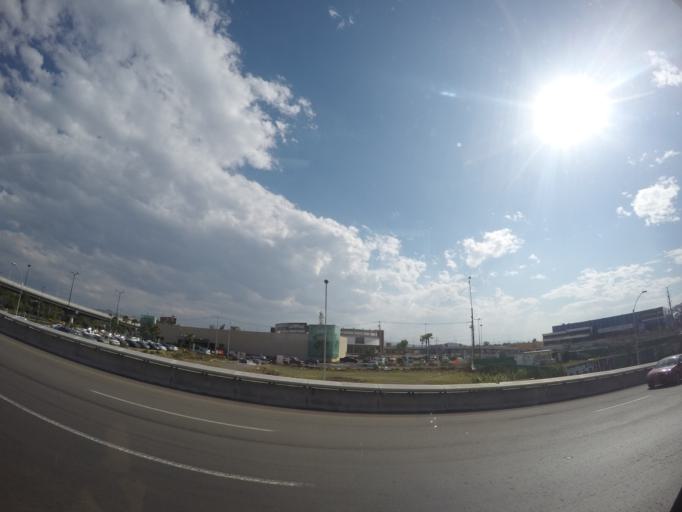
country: MX
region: Queretaro
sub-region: Queretaro
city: Santiago de Queretaro
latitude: 20.5767
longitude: -100.4049
